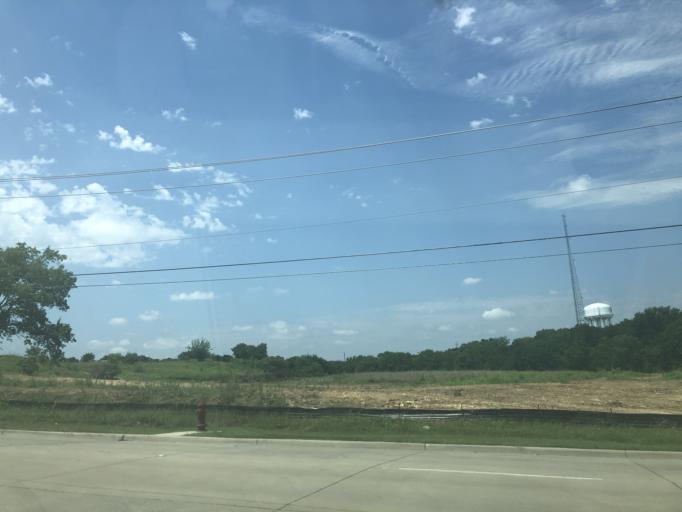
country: US
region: Texas
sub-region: Dallas County
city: Grand Prairie
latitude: 32.7231
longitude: -97.0151
